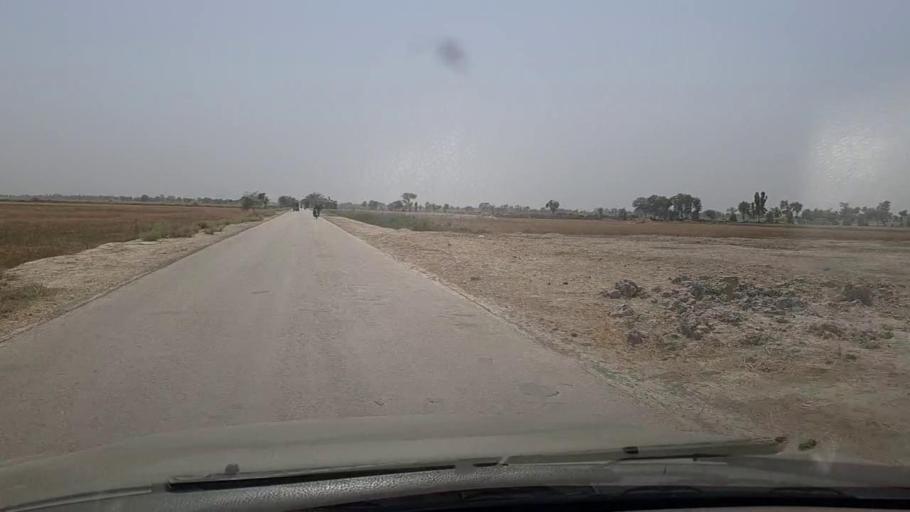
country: PK
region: Sindh
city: Miro Khan
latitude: 27.6970
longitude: 68.0594
